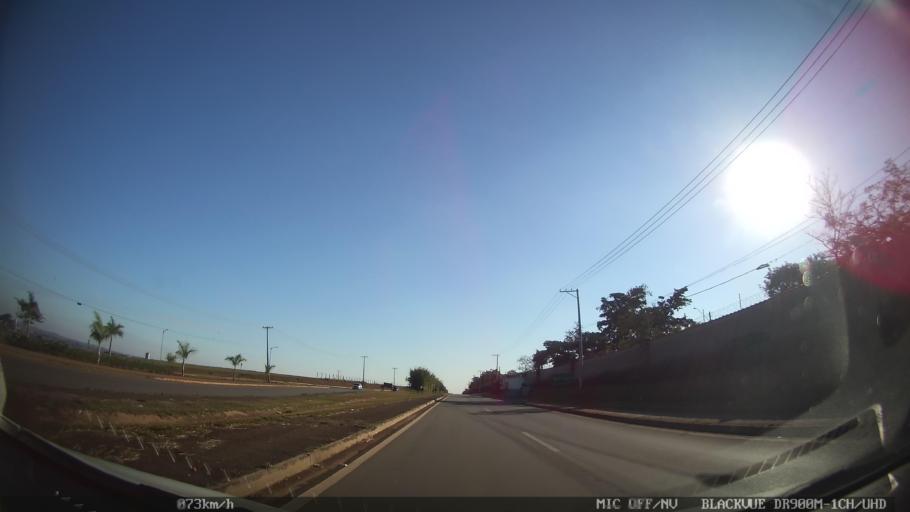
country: BR
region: Sao Paulo
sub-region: Nova Odessa
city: Nova Odessa
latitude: -22.7667
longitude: -47.2664
